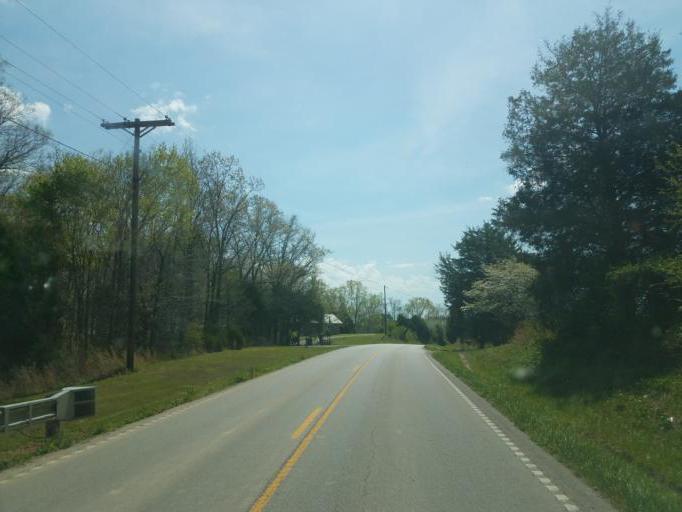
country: US
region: Kentucky
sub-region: Edmonson County
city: Brownsville
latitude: 37.1606
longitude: -86.4140
